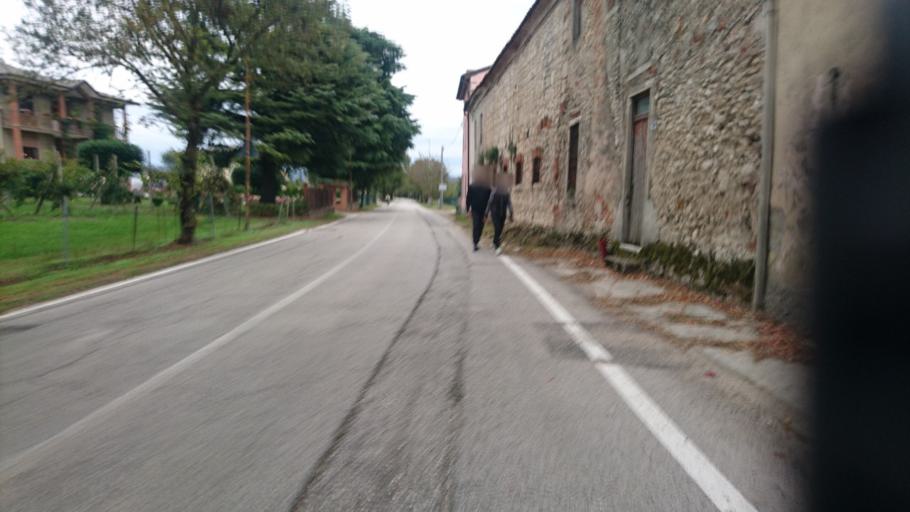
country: IT
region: Veneto
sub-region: Provincia di Vicenza
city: Montecchio Maggiore-Alte Ceccato
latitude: 45.5096
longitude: 11.4248
